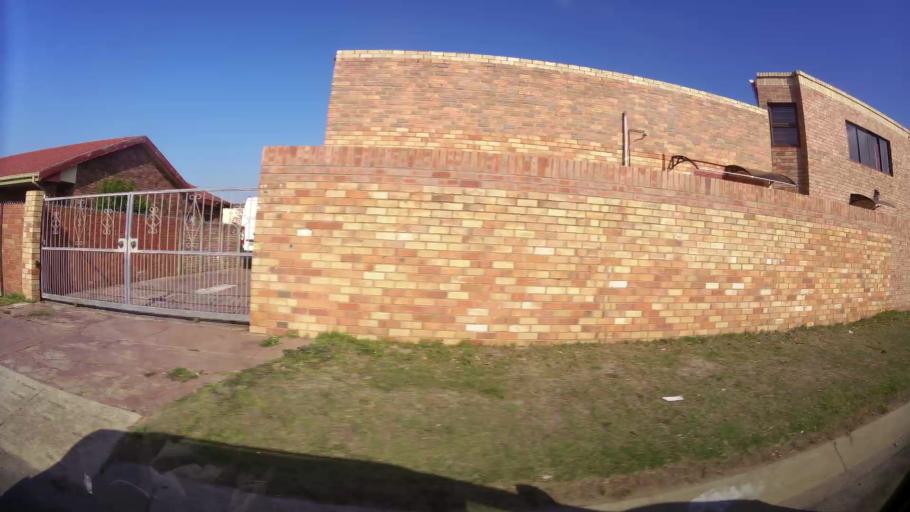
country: ZA
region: Eastern Cape
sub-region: Nelson Mandela Bay Metropolitan Municipality
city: Port Elizabeth
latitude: -33.9213
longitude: 25.5286
